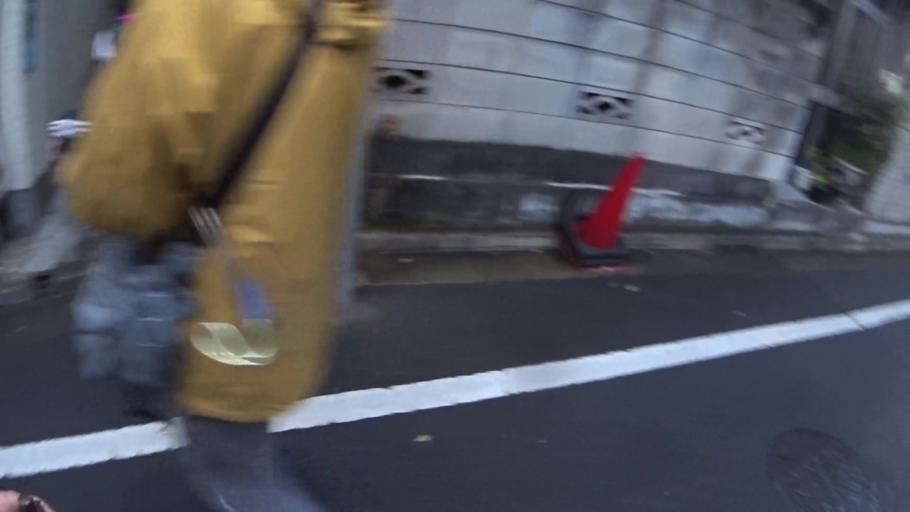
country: JP
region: Tokyo
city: Tokyo
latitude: 35.6895
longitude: 139.7222
